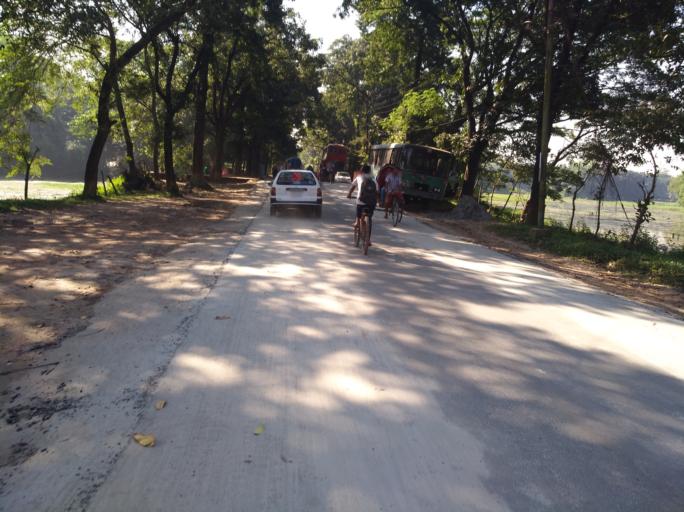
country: BD
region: Dhaka
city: Tungi
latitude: 23.8841
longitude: 90.2679
